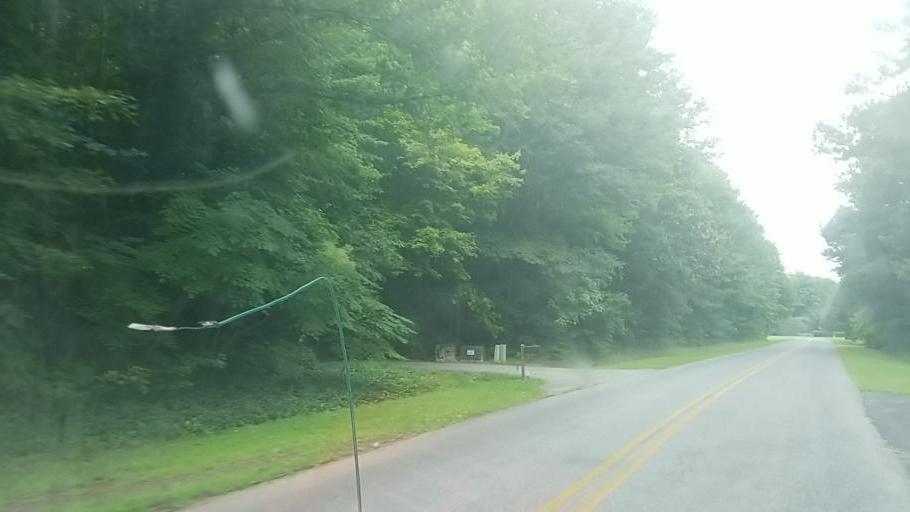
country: US
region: Maryland
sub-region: Worcester County
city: Ocean Pines
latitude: 38.4117
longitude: -75.1837
